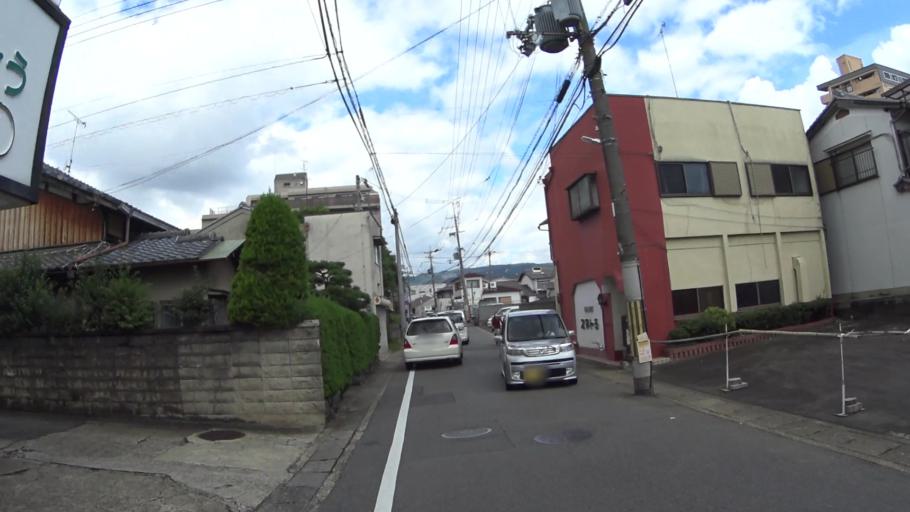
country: JP
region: Shiga Prefecture
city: Otsu-shi
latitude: 34.9760
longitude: 135.8147
